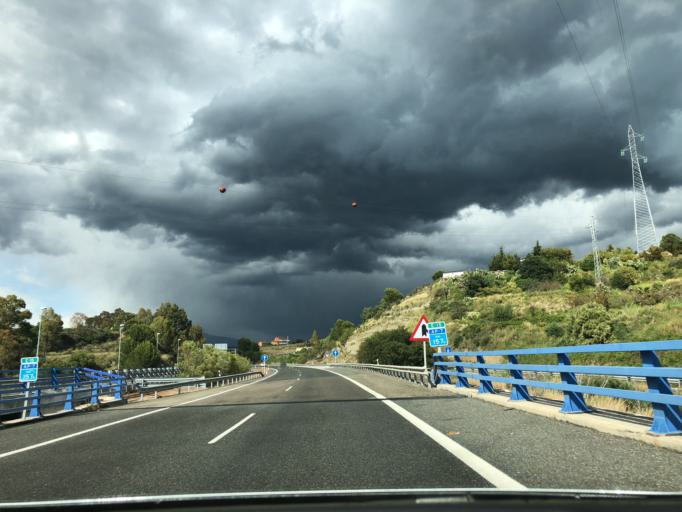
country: ES
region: Andalusia
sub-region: Provincia de Malaga
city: Estepona
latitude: 36.4380
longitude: -5.1347
